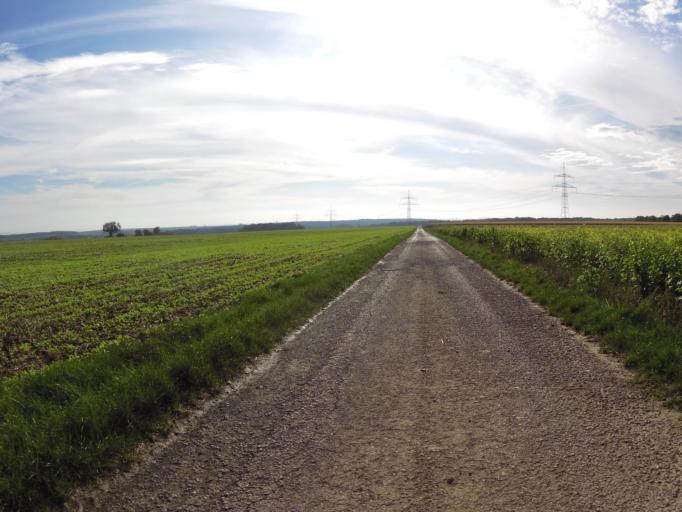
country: DE
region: Bavaria
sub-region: Regierungsbezirk Unterfranken
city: Sommerhausen
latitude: 49.7184
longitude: 10.0620
